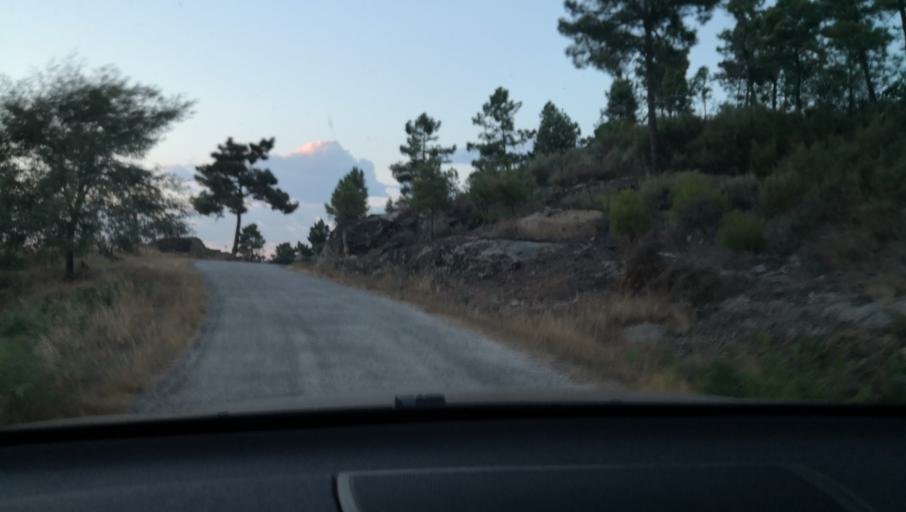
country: PT
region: Vila Real
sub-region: Sabrosa
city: Sabrosa
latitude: 41.2744
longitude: -7.6262
